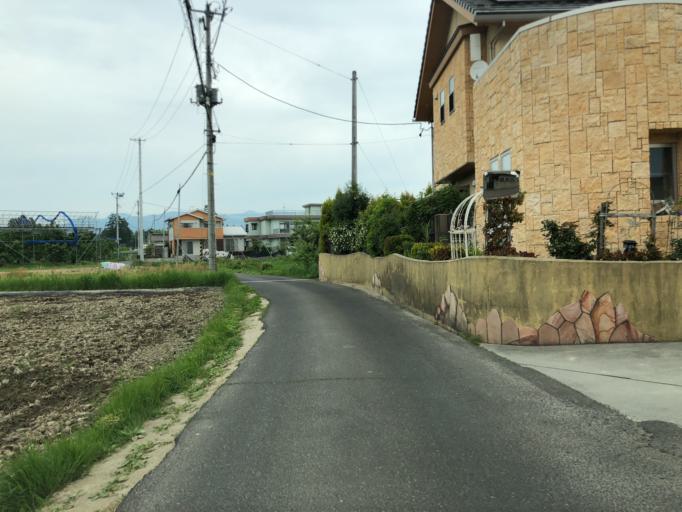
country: JP
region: Fukushima
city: Fukushima-shi
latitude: 37.7985
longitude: 140.4519
